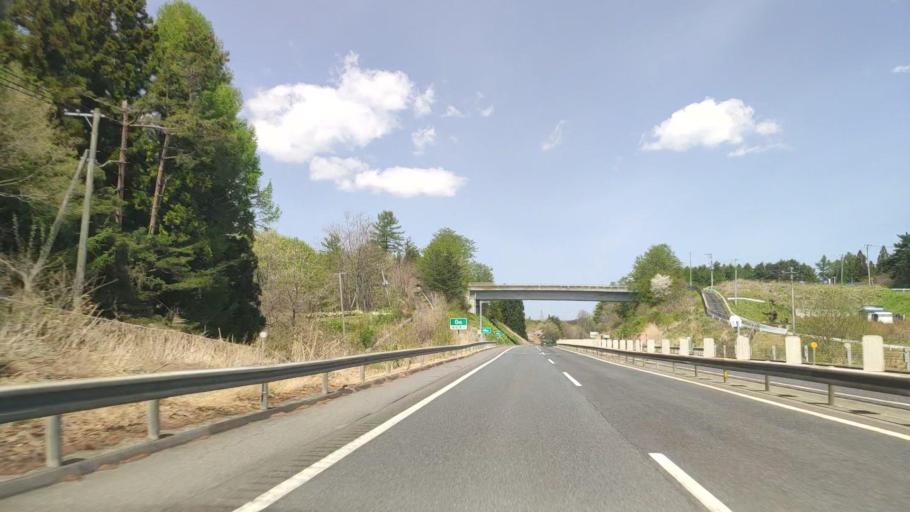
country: JP
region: Aomori
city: Hachinohe
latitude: 40.4155
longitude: 141.4420
